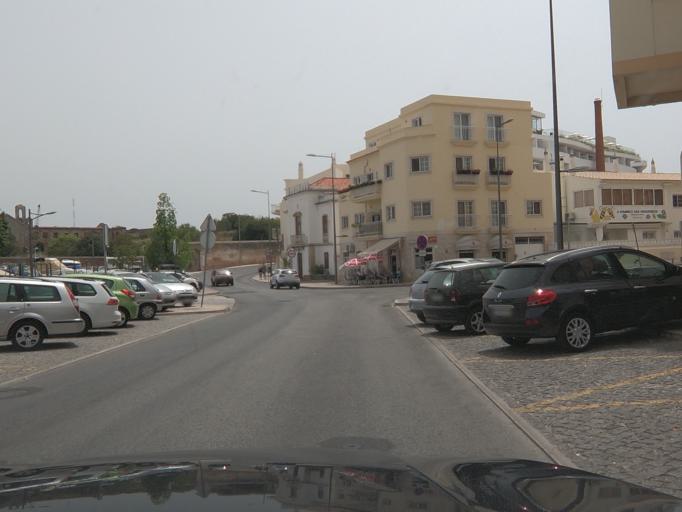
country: PT
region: Faro
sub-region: Portimao
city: Portimao
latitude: 37.1300
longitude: -8.5342
